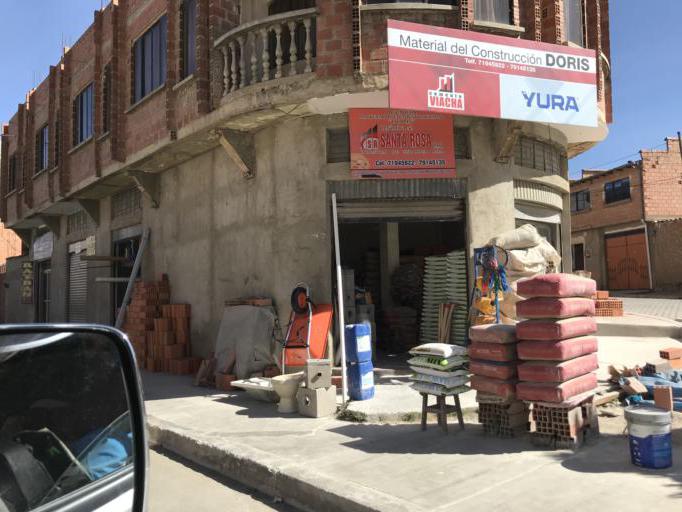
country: BO
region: La Paz
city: La Paz
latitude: -16.4868
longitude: -68.1818
